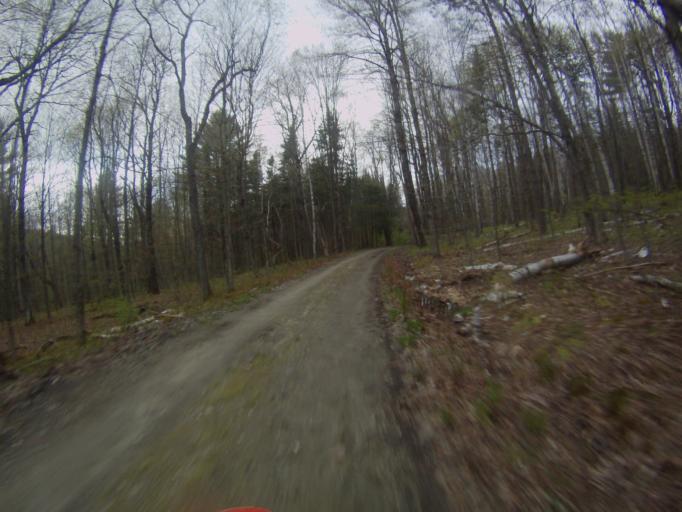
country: US
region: Vermont
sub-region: Addison County
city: Bristol
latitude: 44.0611
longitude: -73.0503
